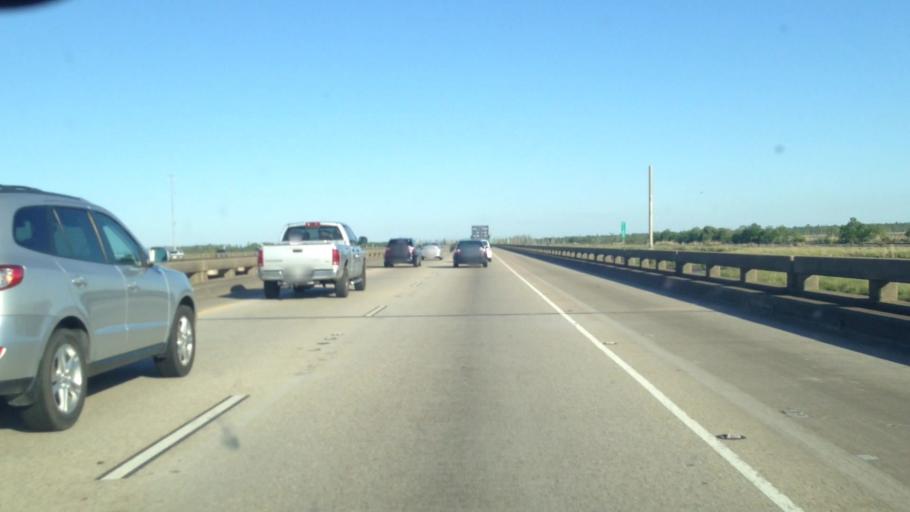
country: US
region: Louisiana
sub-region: Saint Charles Parish
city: Ama
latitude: 30.0184
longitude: -90.3174
